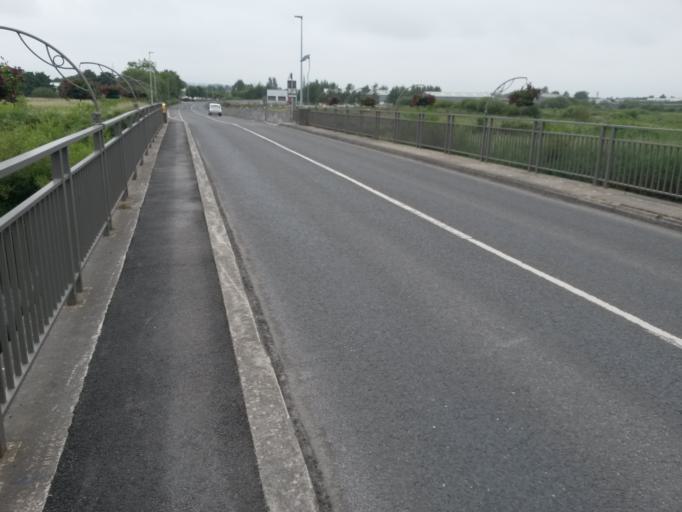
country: IE
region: Munster
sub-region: An Clar
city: Ennis
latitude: 52.8387
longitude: -8.9667
